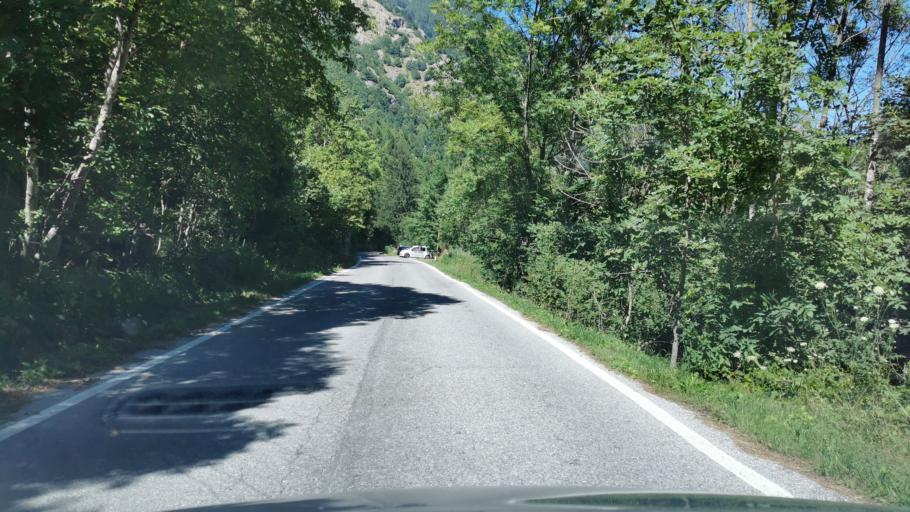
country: IT
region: Piedmont
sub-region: Provincia di Cuneo
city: Demonte
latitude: 44.2399
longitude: 7.3176
